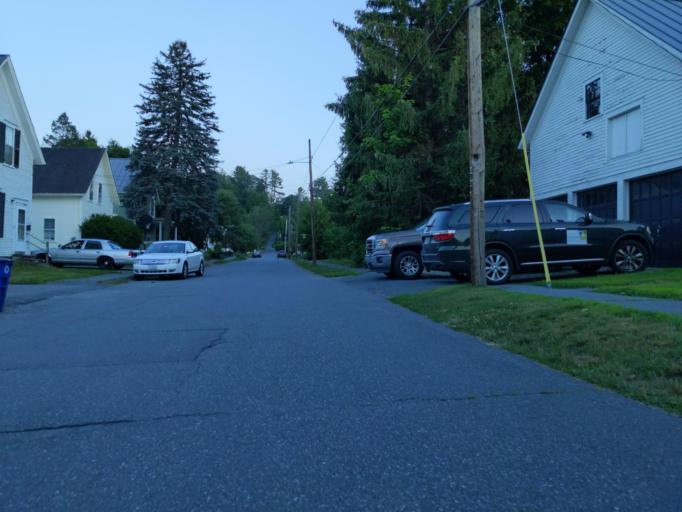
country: US
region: New Hampshire
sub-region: Grafton County
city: Lebanon
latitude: 43.6419
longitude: -72.2467
